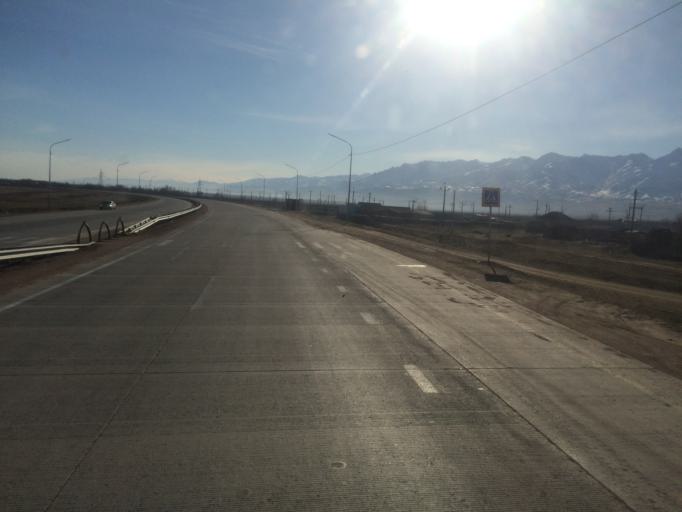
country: KG
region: Talas
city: Ivanovo-Alekseyevka
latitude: 42.9913
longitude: 72.1140
